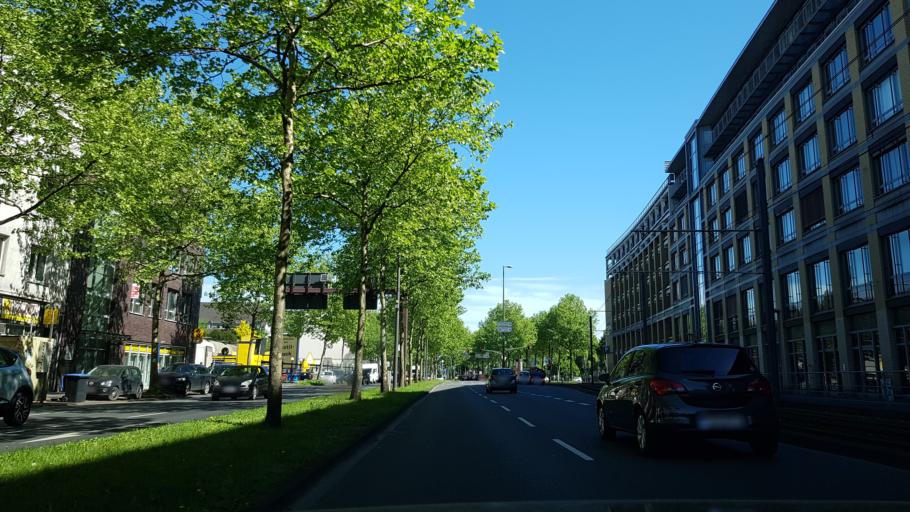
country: DE
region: North Rhine-Westphalia
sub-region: Regierungsbezirk Koln
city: Muelheim
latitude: 50.9626
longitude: 7.0046
